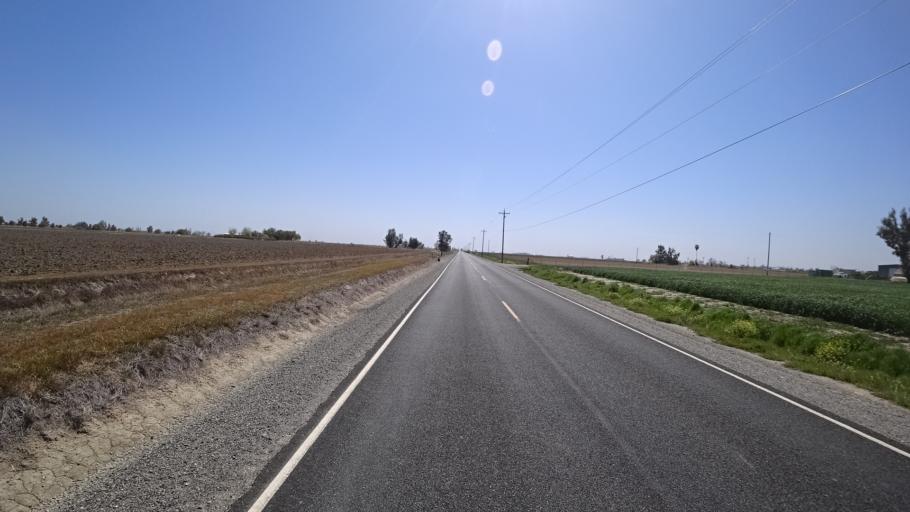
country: US
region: California
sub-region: Glenn County
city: Willows
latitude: 39.5336
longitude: -122.1367
